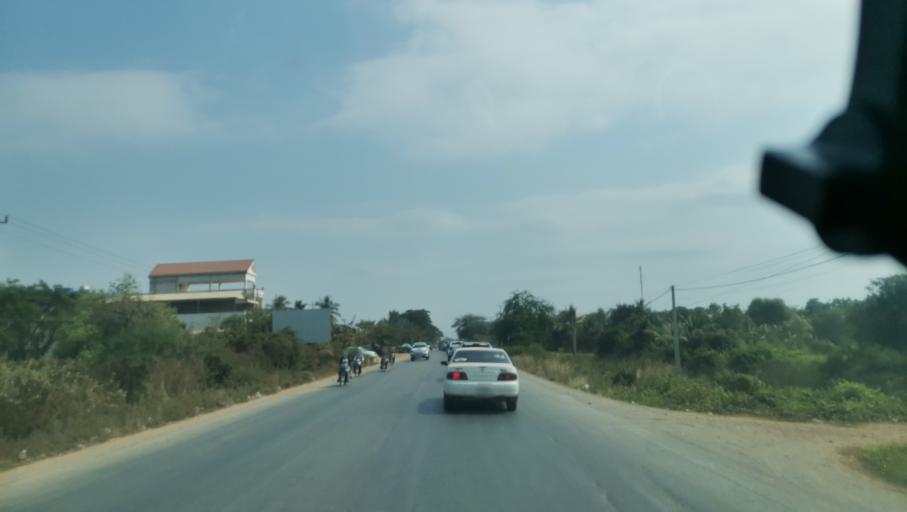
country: KH
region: Battambang
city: Battambang
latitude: 13.0744
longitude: 103.1749
